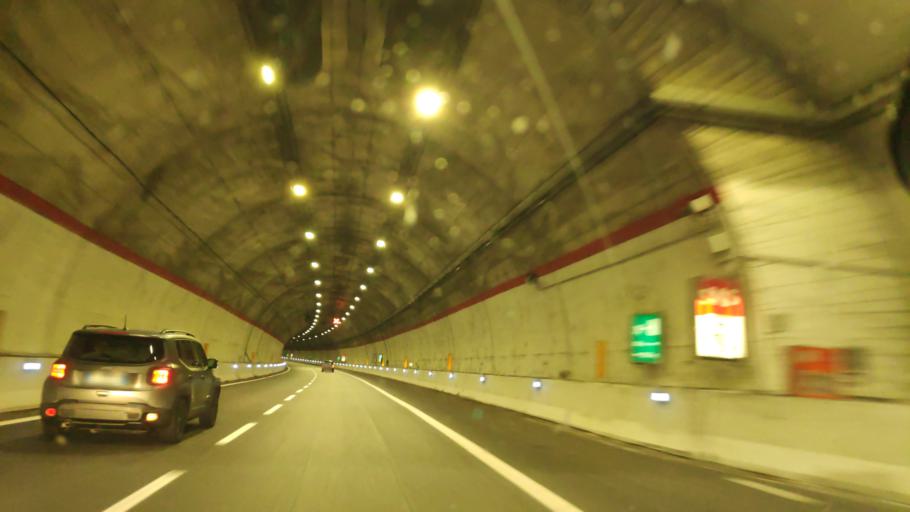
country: IT
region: Campania
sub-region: Provincia di Salerno
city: Sicignano degli Alburni
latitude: 40.6030
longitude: 15.3026
